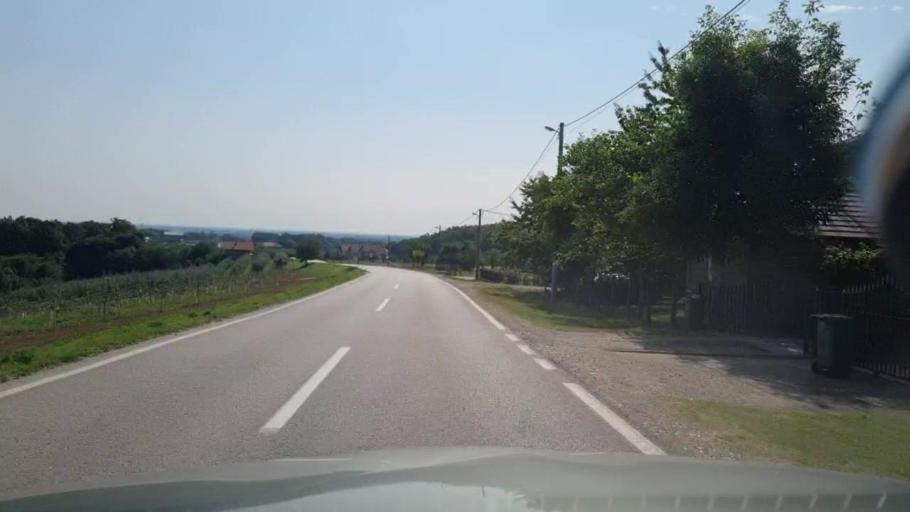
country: BA
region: Federation of Bosnia and Herzegovina
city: Mionica
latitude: 44.8699
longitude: 18.4895
